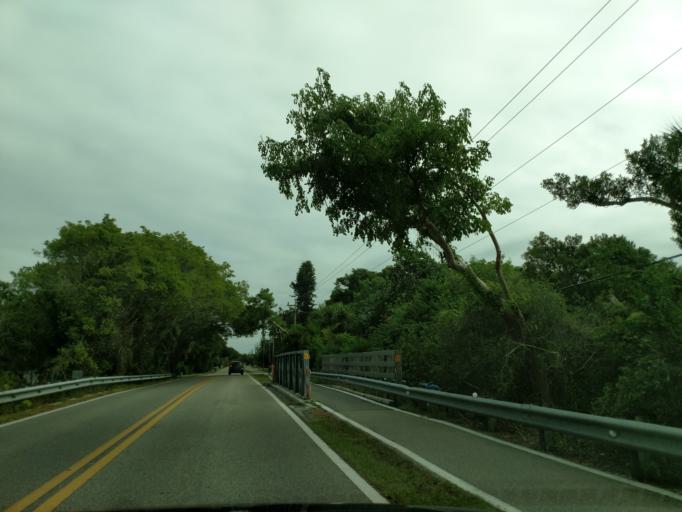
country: US
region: Florida
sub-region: Lee County
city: Sanibel
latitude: 26.4491
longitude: -82.0317
